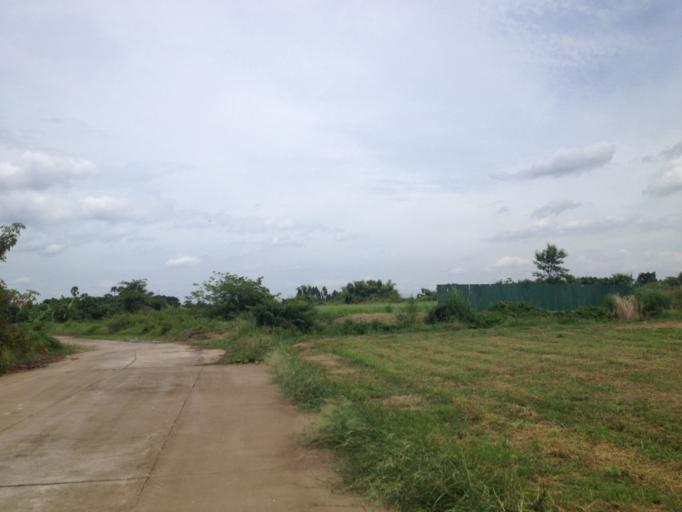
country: TH
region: Chiang Mai
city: Hang Dong
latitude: 18.7113
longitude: 98.9079
